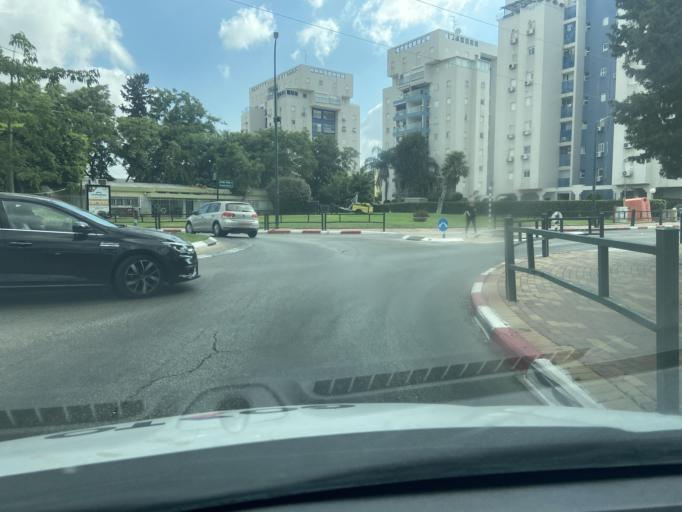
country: IL
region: Central District
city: Yehud
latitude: 32.0339
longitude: 34.8860
